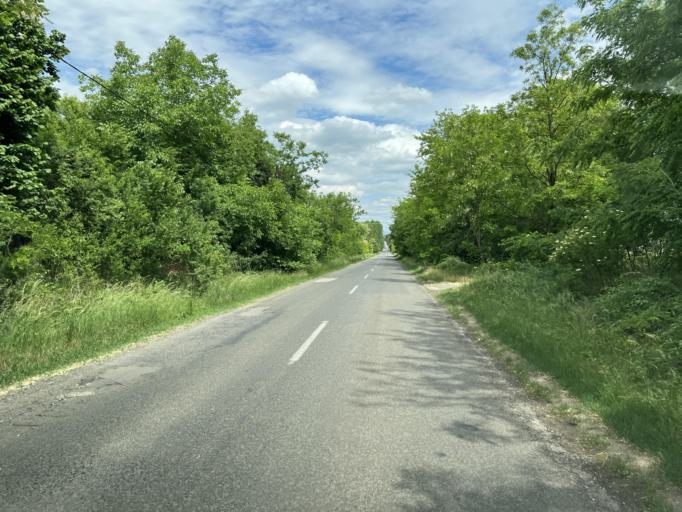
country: HU
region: Pest
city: Toalmas
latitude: 47.4981
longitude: 19.6535
